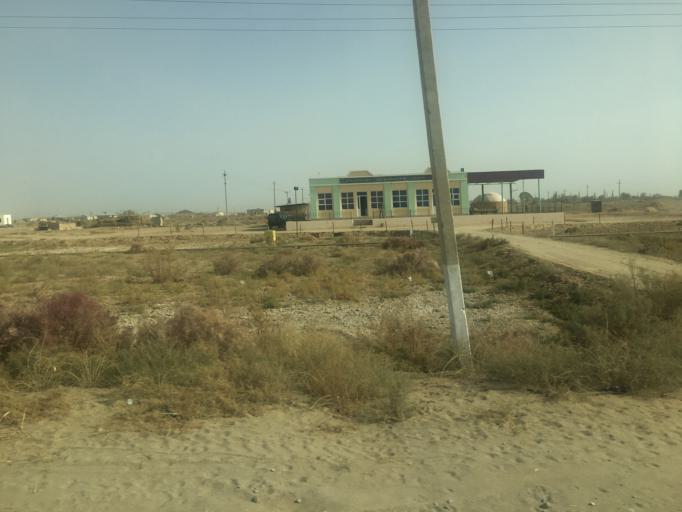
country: TM
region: Lebap
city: Gazojak
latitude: 41.1520
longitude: 61.3978
